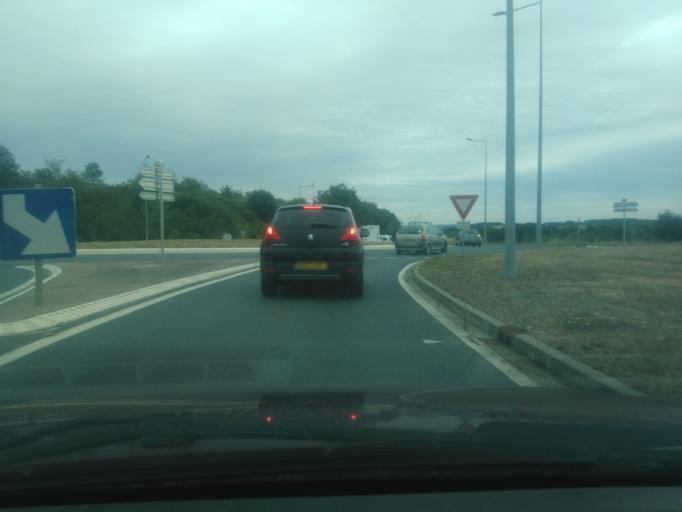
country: FR
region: Centre
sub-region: Departement de l'Indre
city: Saint-Gaultier
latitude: 46.6427
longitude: 1.4246
